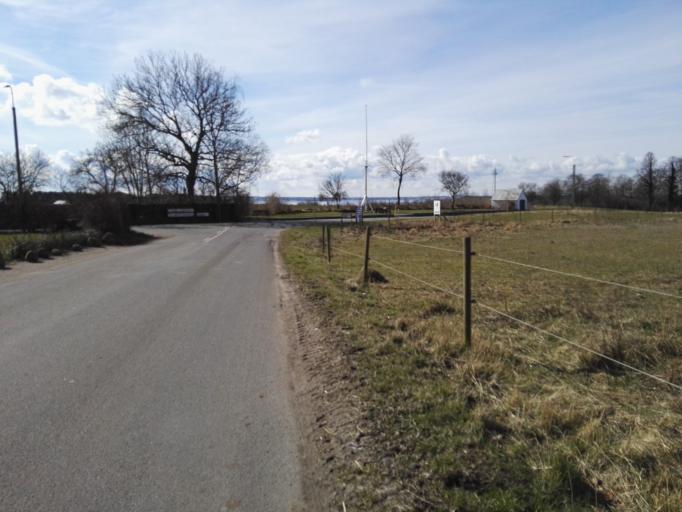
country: DK
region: Zealand
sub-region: Lejre Kommune
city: Ejby
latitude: 55.7668
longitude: 11.8133
